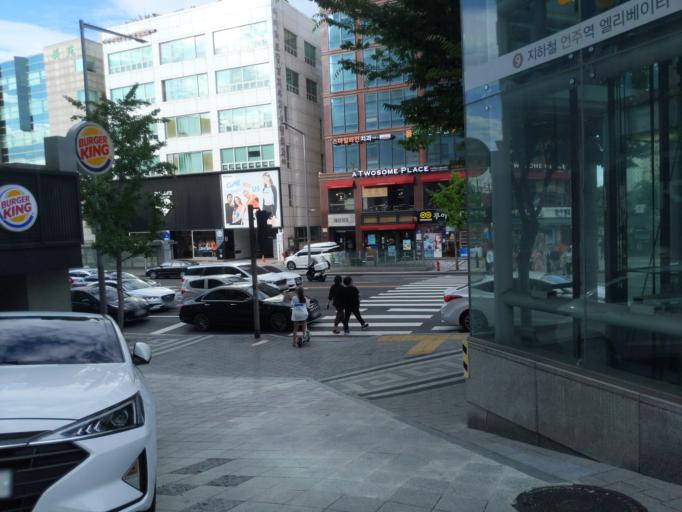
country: KR
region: Seoul
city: Seoul
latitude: 37.5074
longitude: 127.0334
